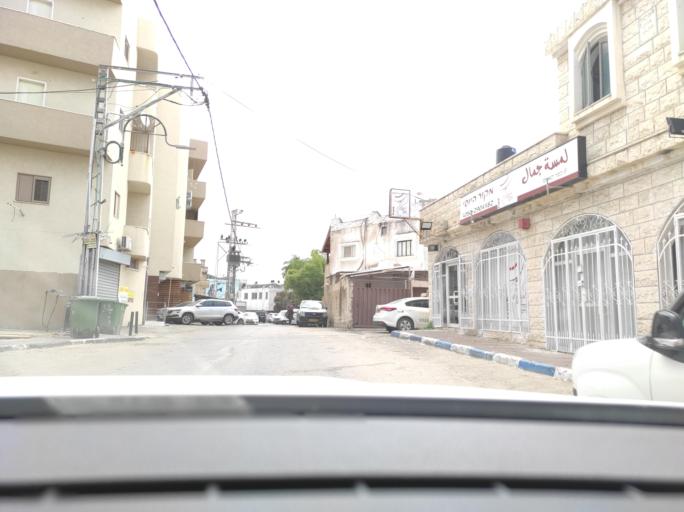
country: IL
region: Central District
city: Kafr Qasim
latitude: 32.1149
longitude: 34.9750
